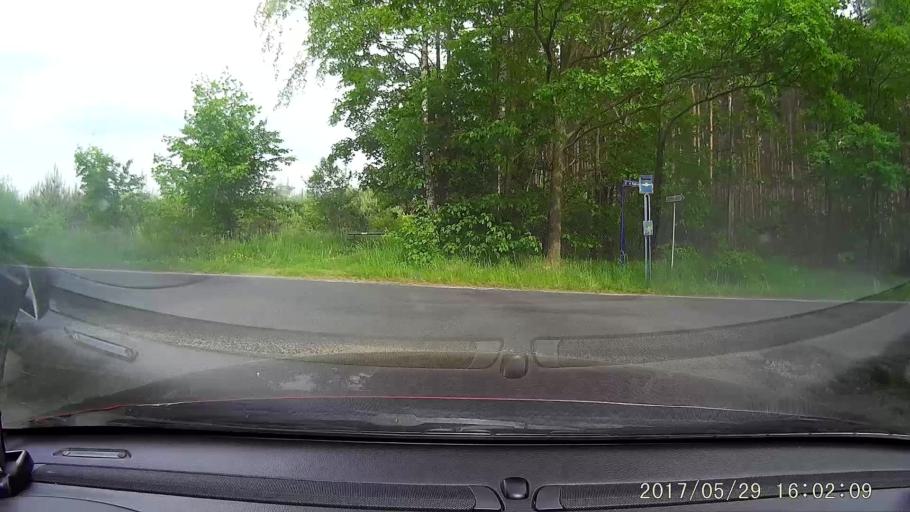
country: PL
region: Lower Silesian Voivodeship
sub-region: Powiat zgorzelecki
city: Wegliniec
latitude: 51.2292
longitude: 15.2077
